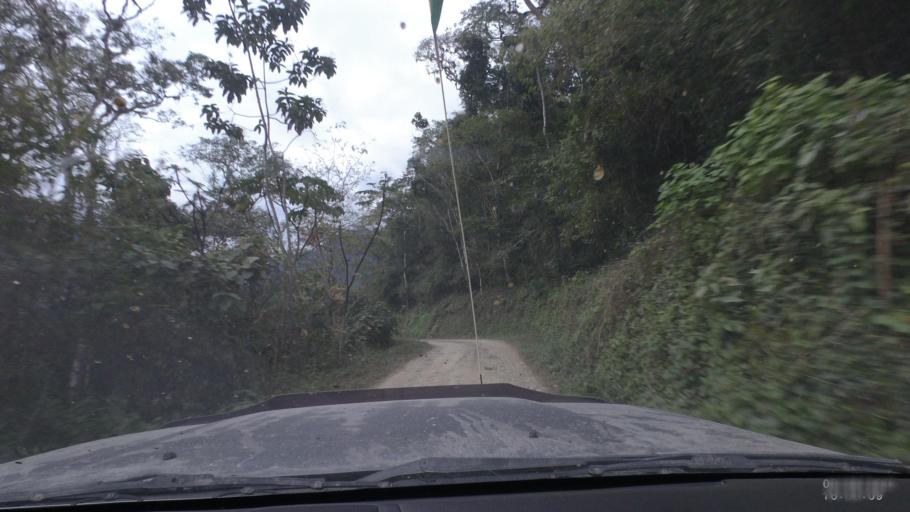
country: BO
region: La Paz
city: Quime
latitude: -16.5276
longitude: -66.7614
